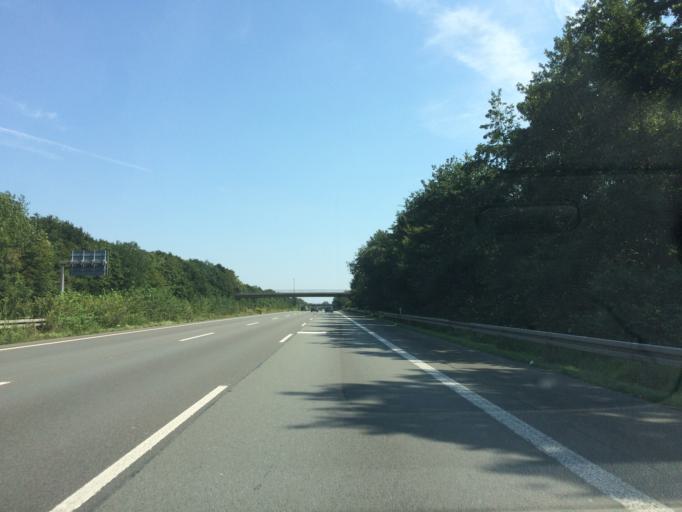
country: DE
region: North Rhine-Westphalia
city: Oer-Erkenschwick
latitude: 51.5979
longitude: 7.2717
